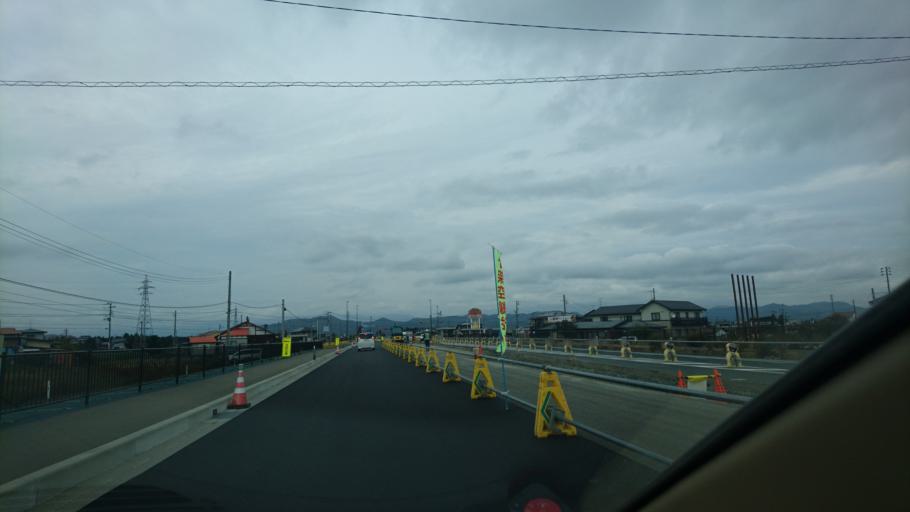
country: JP
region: Iwate
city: Morioka-shi
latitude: 39.6891
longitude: 141.1134
